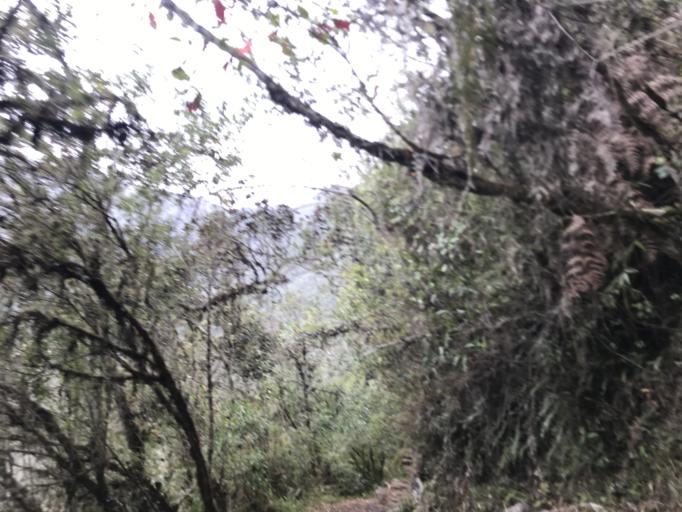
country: PE
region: Cusco
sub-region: Provincia de La Convencion
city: Santa Teresa
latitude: -13.1763
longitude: -72.5361
